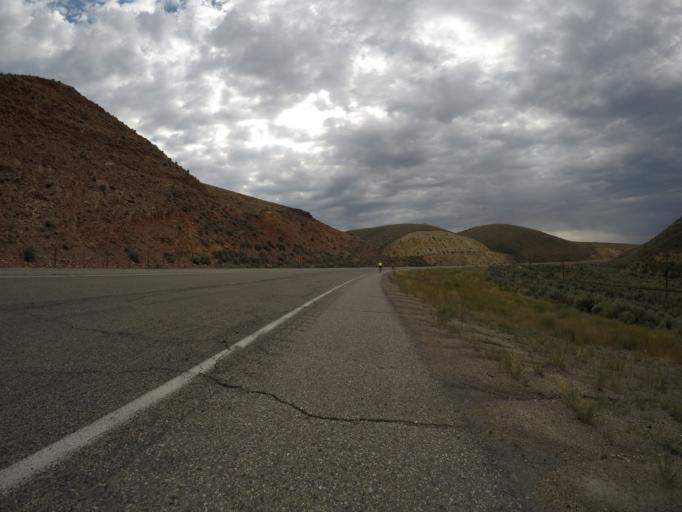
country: US
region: Wyoming
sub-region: Lincoln County
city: Kemmerer
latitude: 41.8261
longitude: -110.8121
